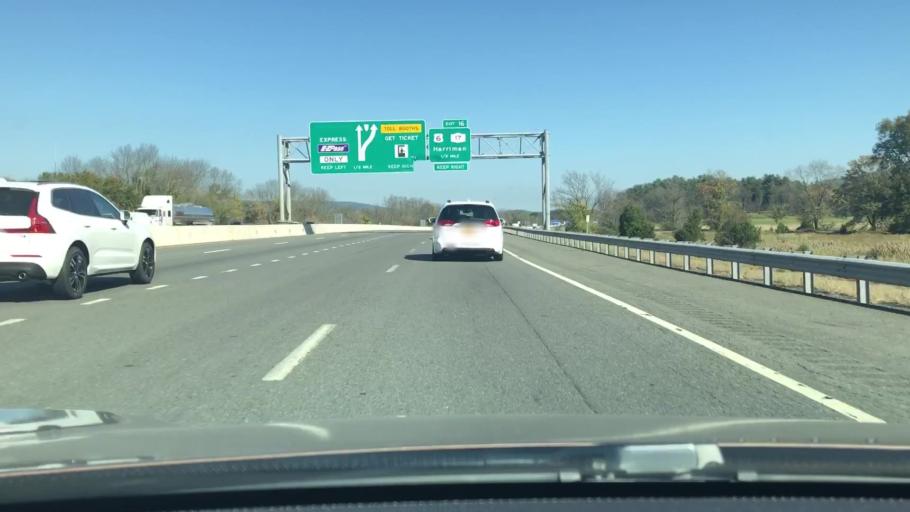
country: US
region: New York
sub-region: Orange County
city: Harriman
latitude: 41.2943
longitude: -74.1384
